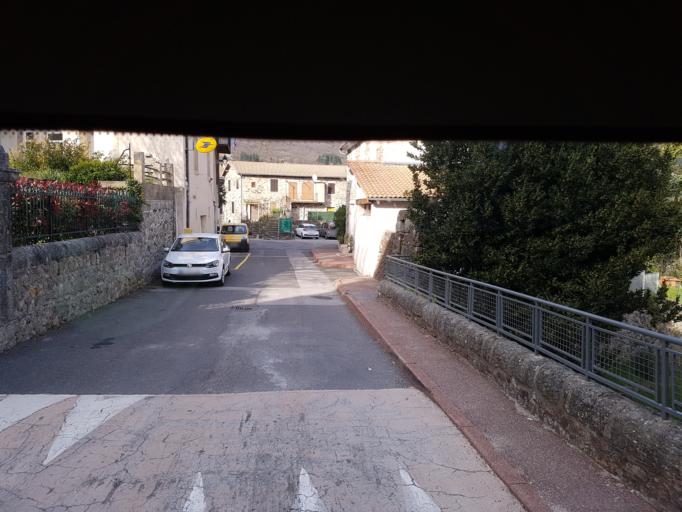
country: FR
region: Languedoc-Roussillon
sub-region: Departement du Gard
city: Branoux-les-Taillades
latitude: 44.3333
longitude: 3.8962
